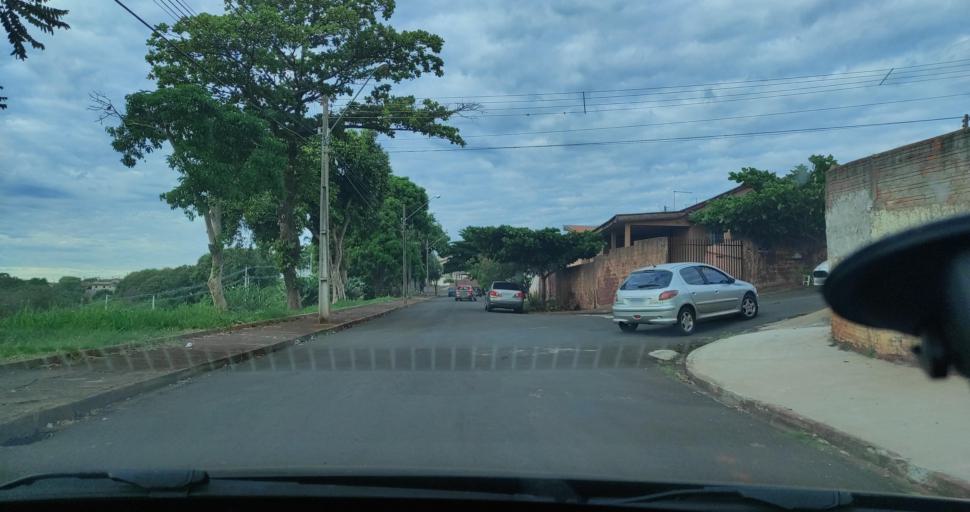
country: BR
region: Parana
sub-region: Ibipora
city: Ibipora
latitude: -23.2550
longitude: -51.0486
